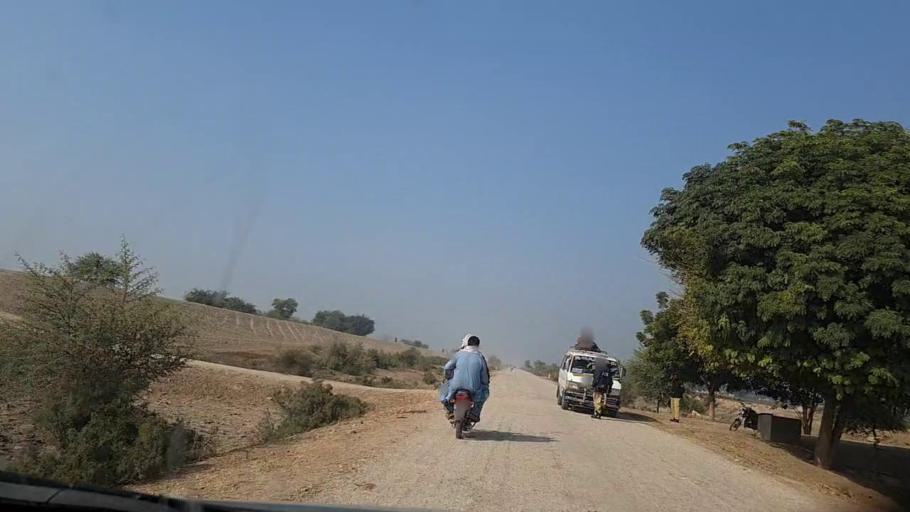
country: PK
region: Sindh
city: Moro
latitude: 26.7156
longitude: 67.9239
